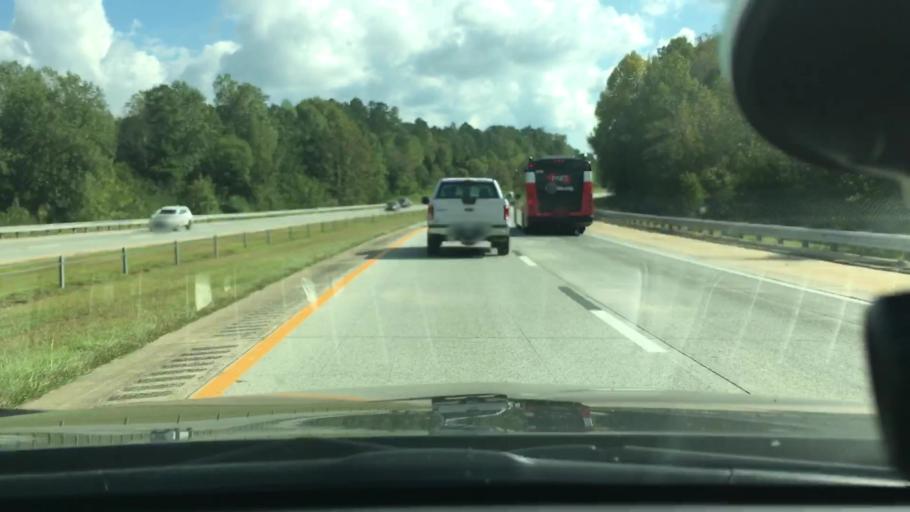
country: US
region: North Carolina
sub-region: Orange County
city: Hillsborough
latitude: 35.9961
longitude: -79.0760
